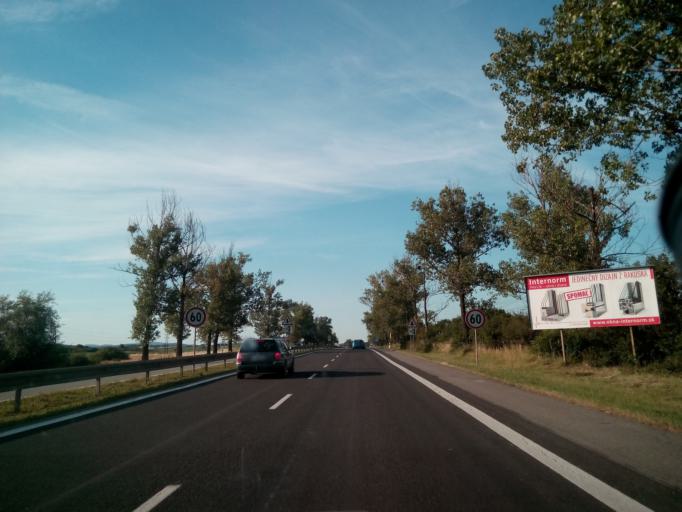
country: SK
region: Kosicky
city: Kosice
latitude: 48.6595
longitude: 21.2069
